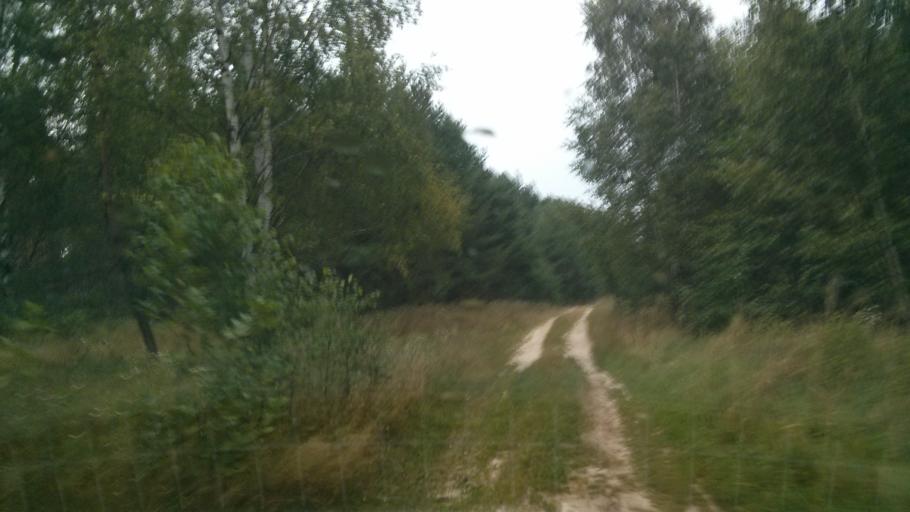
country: RU
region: Nizjnij Novgorod
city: Shimorskoye
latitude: 55.3082
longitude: 41.8566
